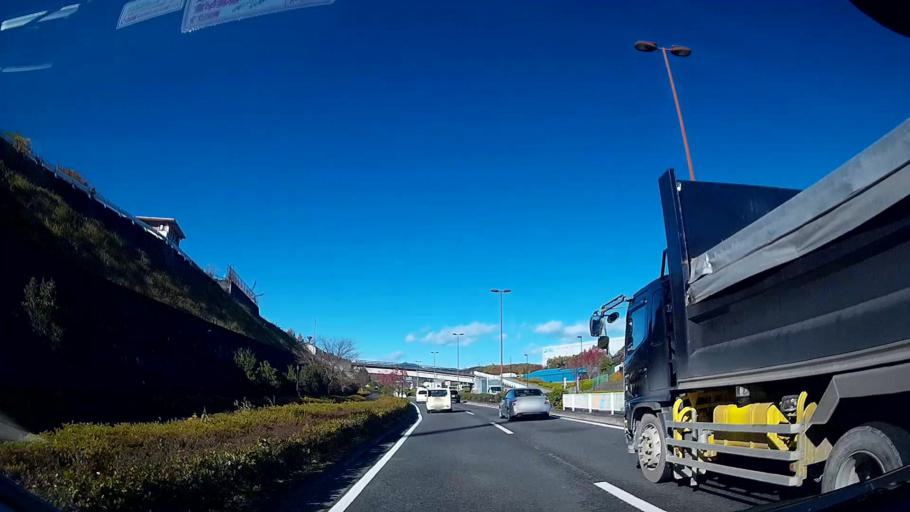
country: JP
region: Tokyo
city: Fussa
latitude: 35.7071
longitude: 139.2954
